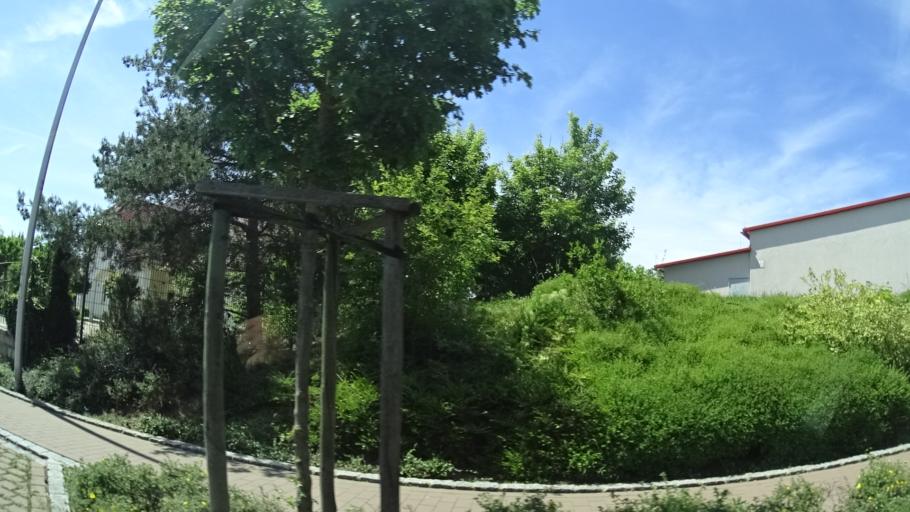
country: DE
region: Bavaria
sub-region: Regierungsbezirk Unterfranken
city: Poppenhausen
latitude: 50.1038
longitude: 10.1435
